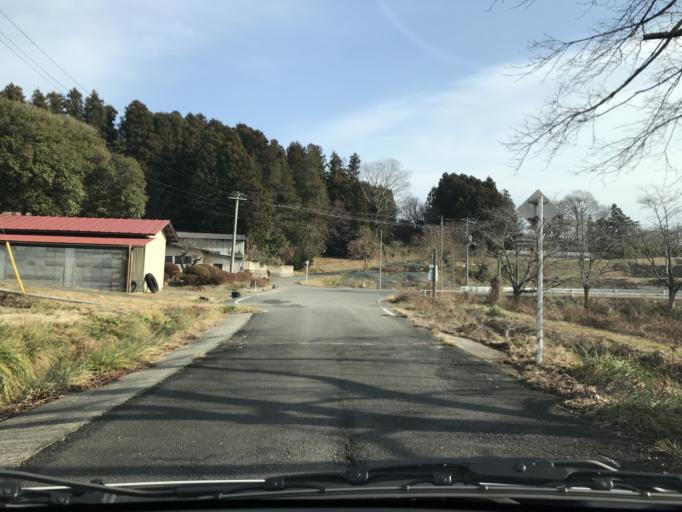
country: JP
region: Miyagi
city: Wakuya
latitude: 38.6955
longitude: 141.1423
